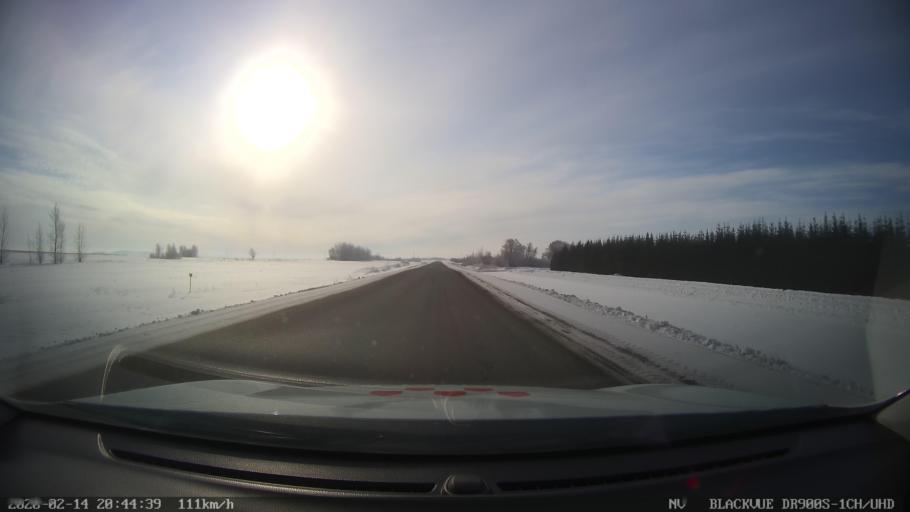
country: RU
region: Tatarstan
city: Kuybyshevskiy Zaton
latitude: 55.2901
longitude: 49.1454
